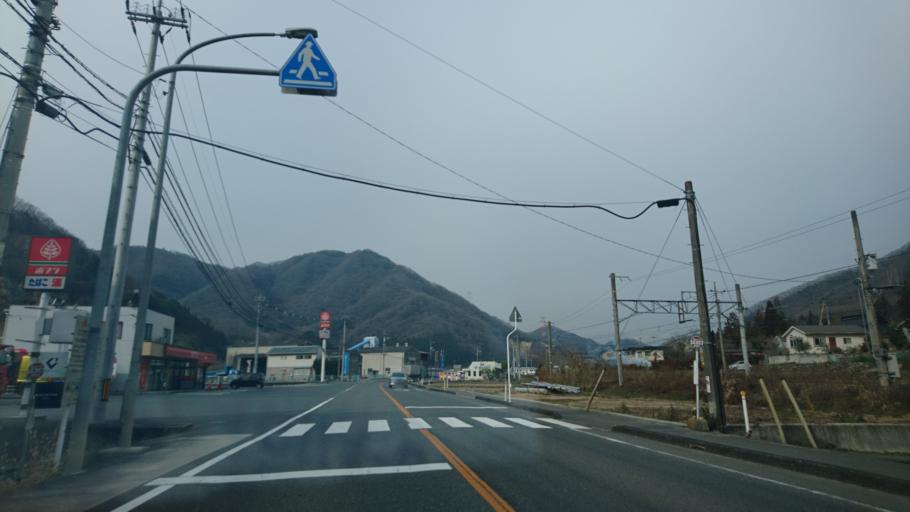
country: JP
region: Okayama
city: Takahashi
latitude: 34.8258
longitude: 133.6129
